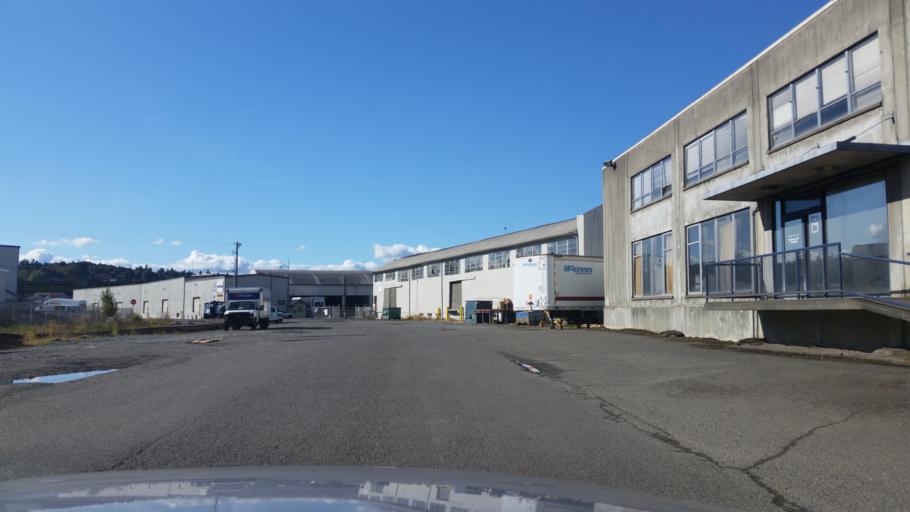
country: US
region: Washington
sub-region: King County
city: Seattle
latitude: 47.6561
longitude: -122.3720
